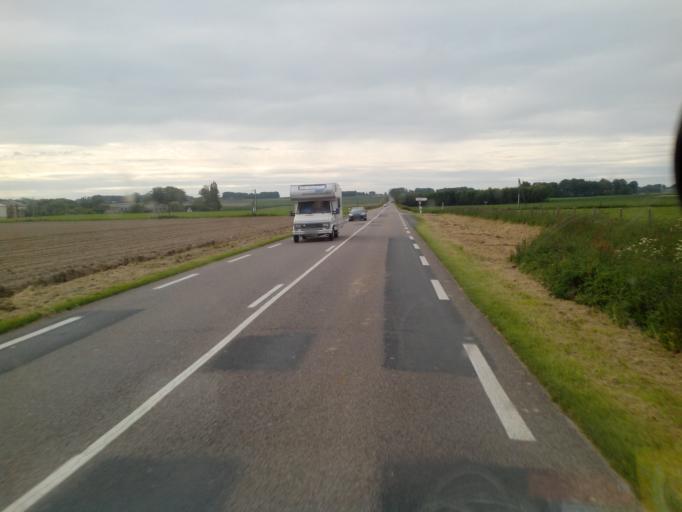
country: FR
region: Haute-Normandie
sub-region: Departement de la Seine-Maritime
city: Fauville-en-Caux
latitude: 49.6714
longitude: 0.5734
